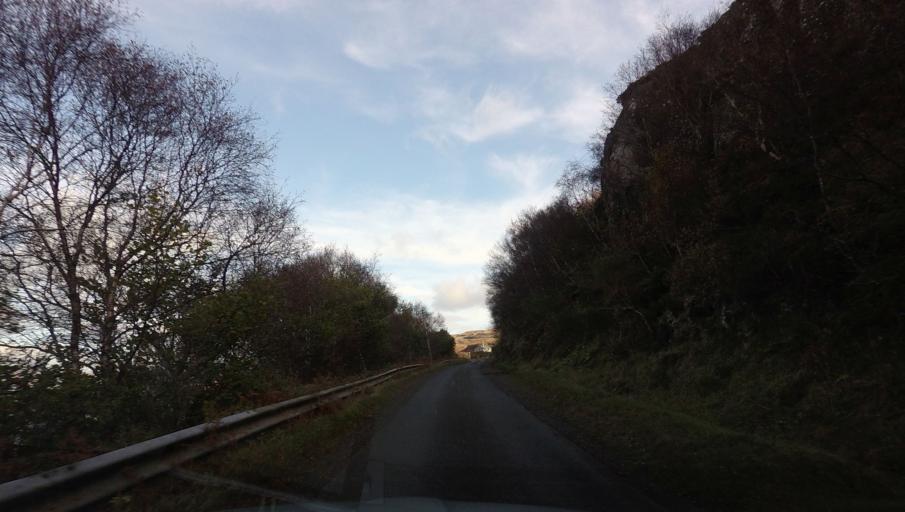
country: GB
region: Scotland
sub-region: Argyll and Bute
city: Isle Of Mull
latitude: 56.3365
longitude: -6.1546
